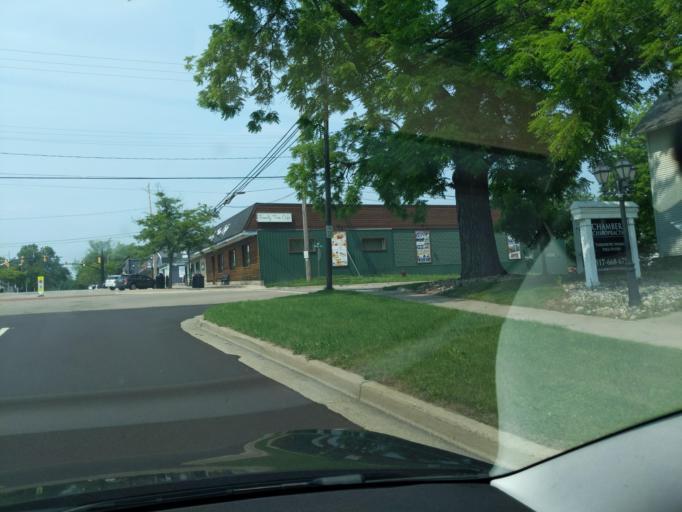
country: US
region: Michigan
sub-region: Clinton County
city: DeWitt
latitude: 42.8411
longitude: -84.5691
